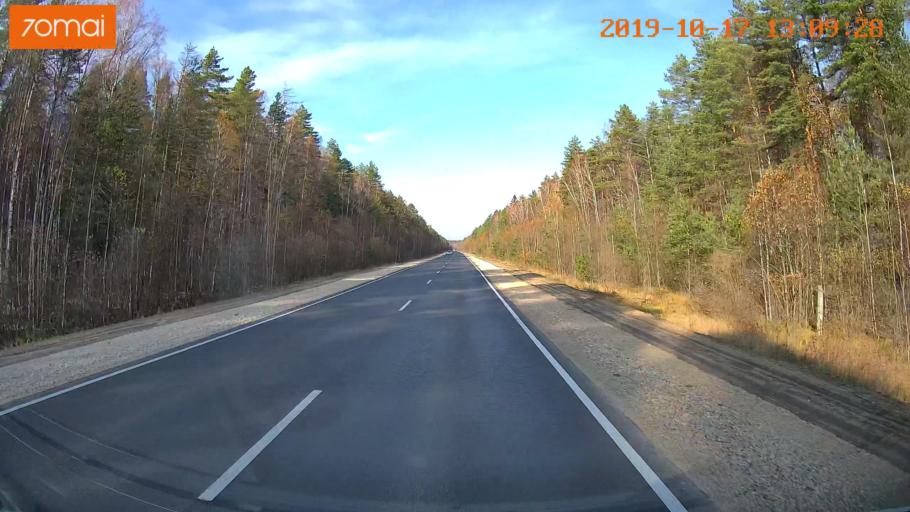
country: RU
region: Rjazan
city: Syntul
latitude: 55.0043
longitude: 41.2629
